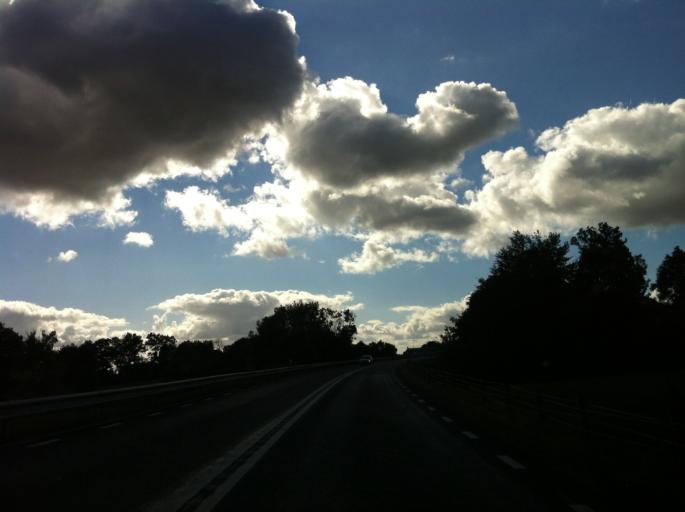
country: SE
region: Skane
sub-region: Tomelilla Kommun
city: Tomelilla
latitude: 55.6543
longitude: 14.0308
